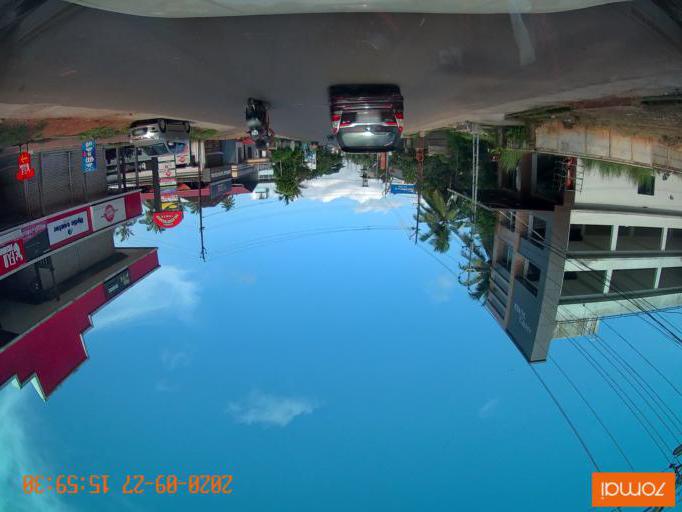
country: IN
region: Kerala
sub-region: Thrissur District
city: Trichur
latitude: 10.5201
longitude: 76.1947
